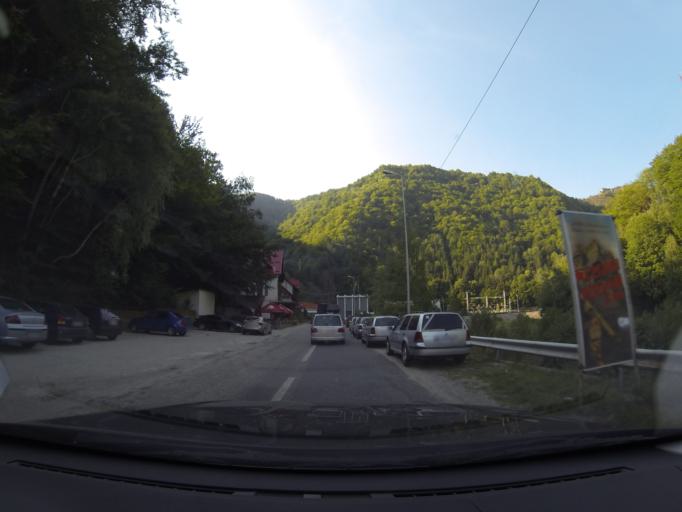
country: RO
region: Arges
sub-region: Comuna Arefu
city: Arefu
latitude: 45.3479
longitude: 24.6325
